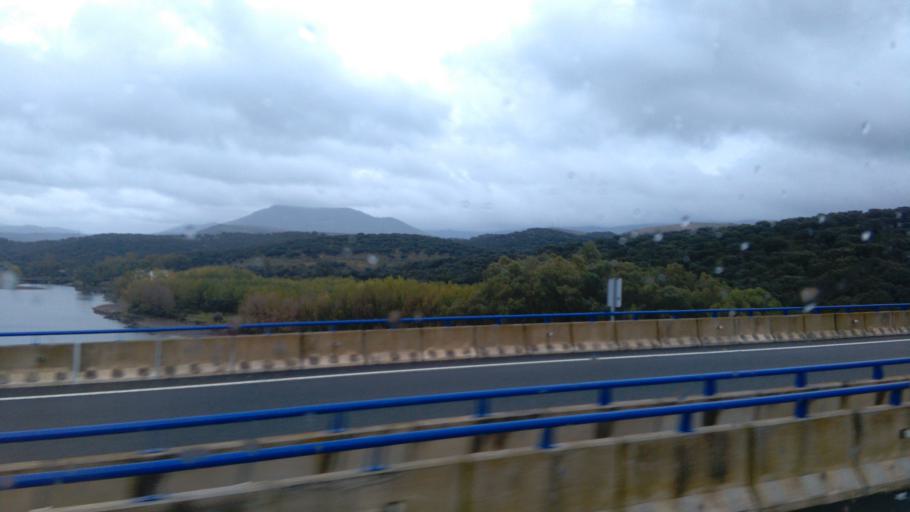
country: ES
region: Extremadura
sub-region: Provincia de Caceres
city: Romangordo
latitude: 39.7804
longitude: -5.7321
